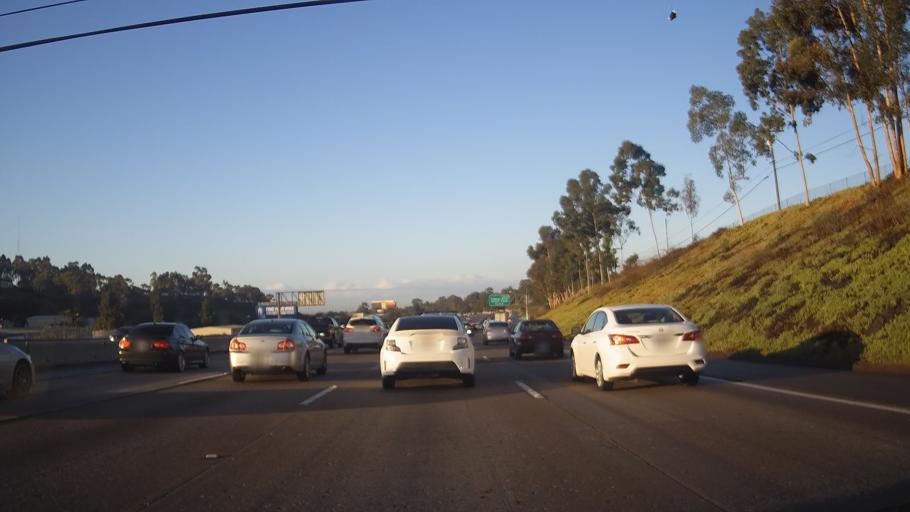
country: US
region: California
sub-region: San Diego County
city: Lemon Grove
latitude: 32.7293
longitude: -117.0646
